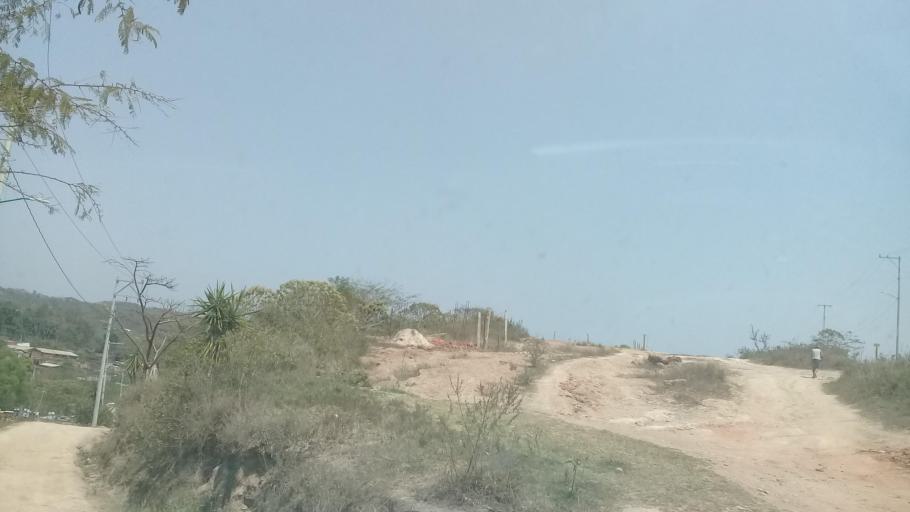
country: MX
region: Veracruz
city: El Castillo
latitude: 19.5495
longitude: -96.8576
